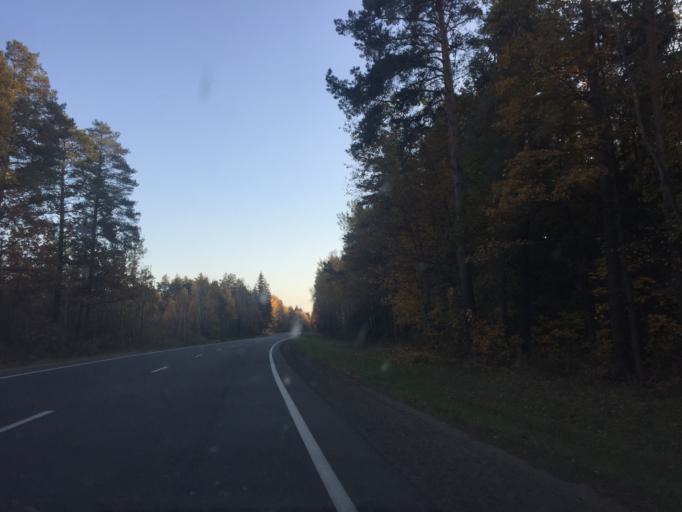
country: BY
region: Mogilev
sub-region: Mahilyowski Rayon
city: Kadino
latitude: 53.8924
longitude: 30.4853
